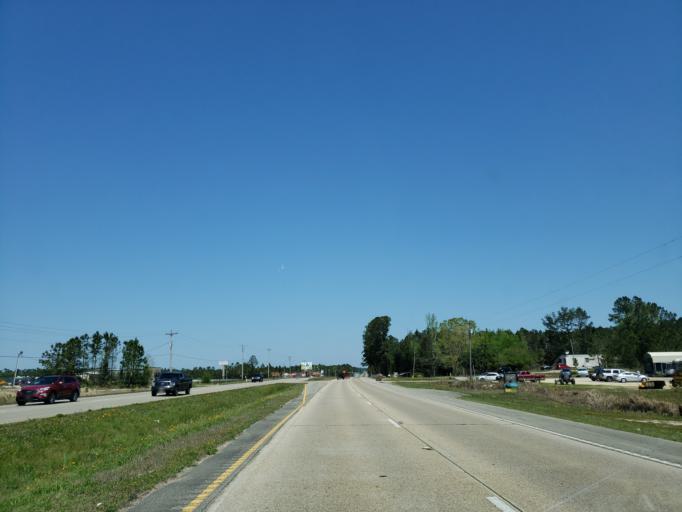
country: US
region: Mississippi
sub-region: Harrison County
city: Lyman
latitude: 30.5500
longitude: -89.1201
